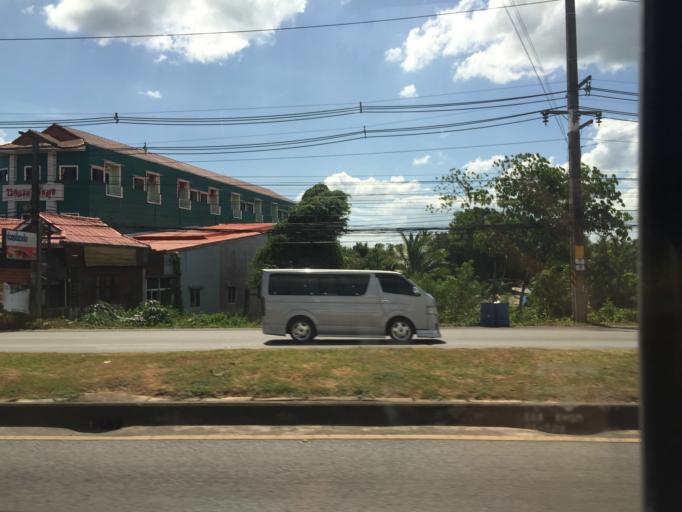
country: TH
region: Krabi
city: Krabi
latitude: 8.1036
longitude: 98.8983
